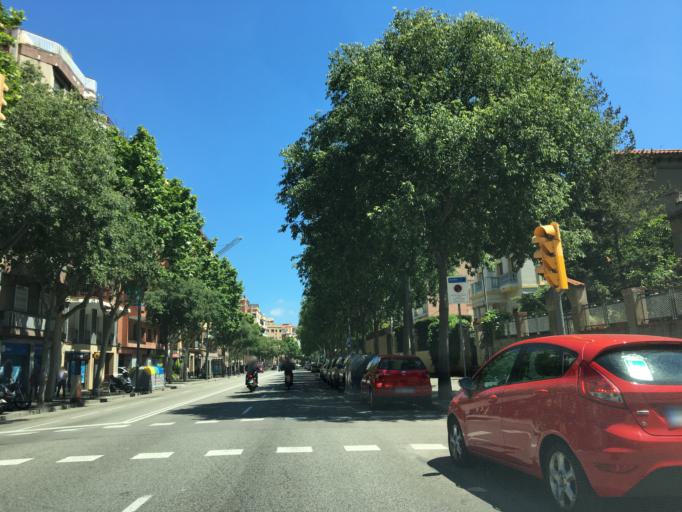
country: ES
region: Catalonia
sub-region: Provincia de Barcelona
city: Horta-Guinardo
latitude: 41.4276
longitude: 2.1673
